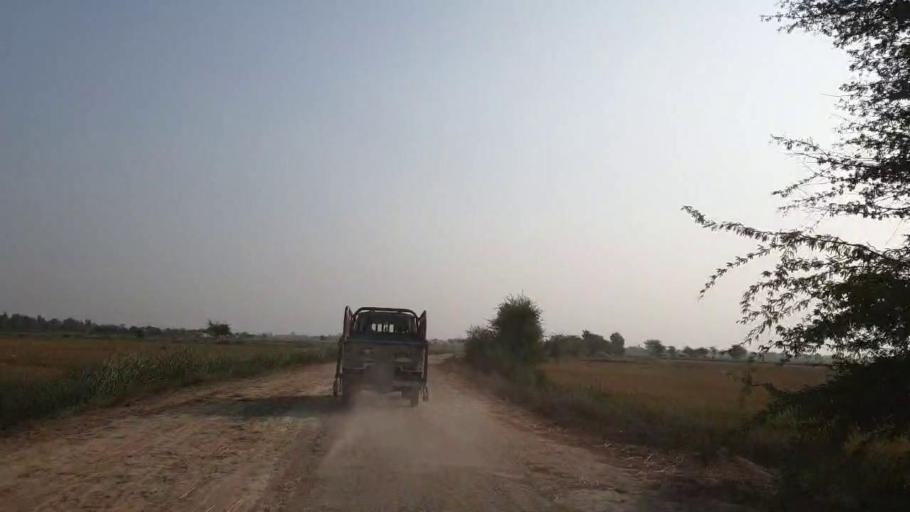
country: PK
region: Sindh
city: Kario
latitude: 24.9082
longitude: 68.5685
